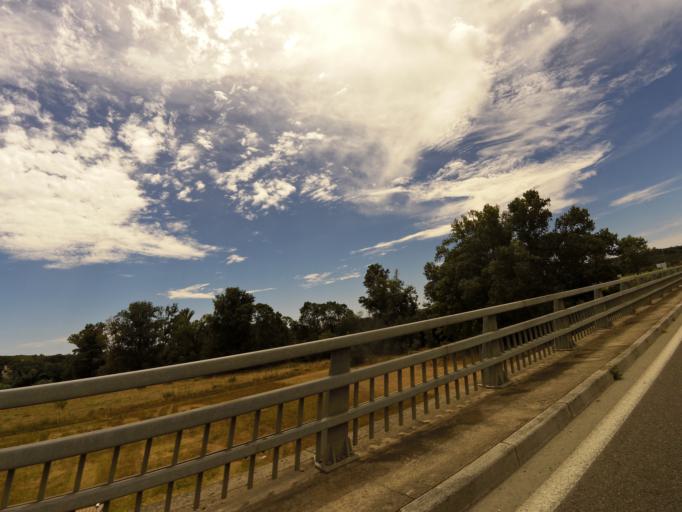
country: FR
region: Languedoc-Roussillon
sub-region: Departement du Gard
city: Quissac
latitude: 43.9046
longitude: 4.0030
